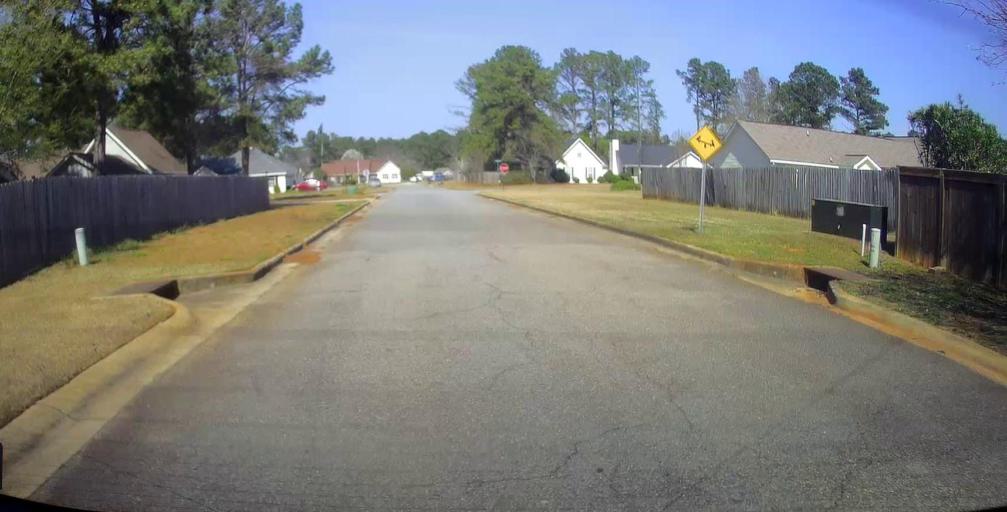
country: US
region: Georgia
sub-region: Houston County
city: Centerville
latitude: 32.5859
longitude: -83.7128
